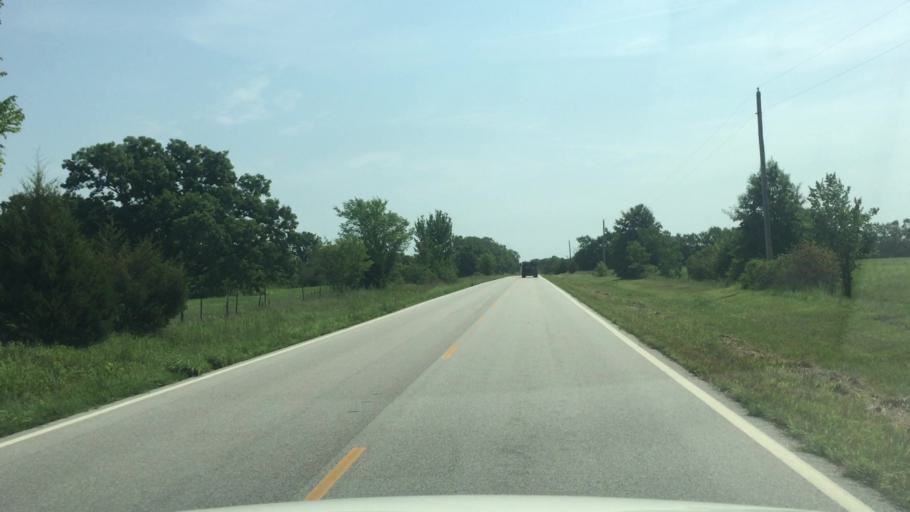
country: US
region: Kansas
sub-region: Montgomery County
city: Cherryvale
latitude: 37.1940
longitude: -95.5476
